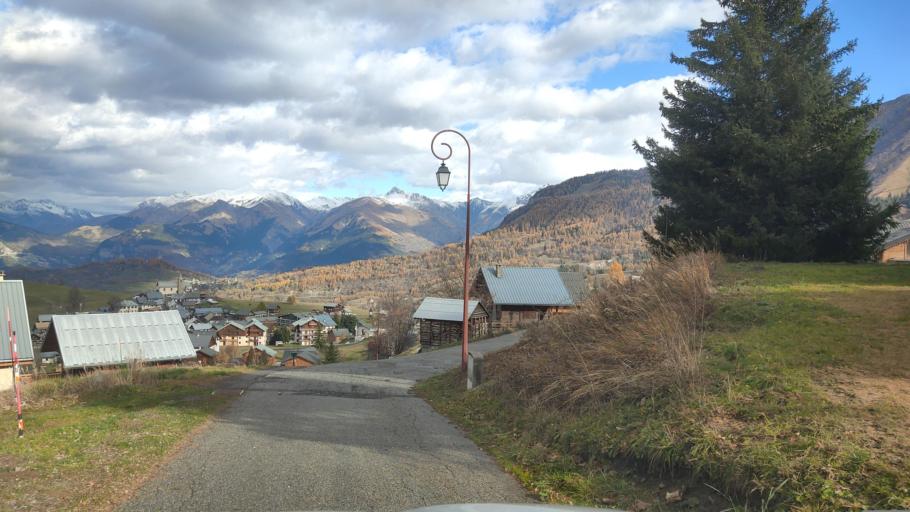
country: FR
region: Rhone-Alpes
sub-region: Departement de la Savoie
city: Villargondran
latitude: 45.2135
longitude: 6.3393
